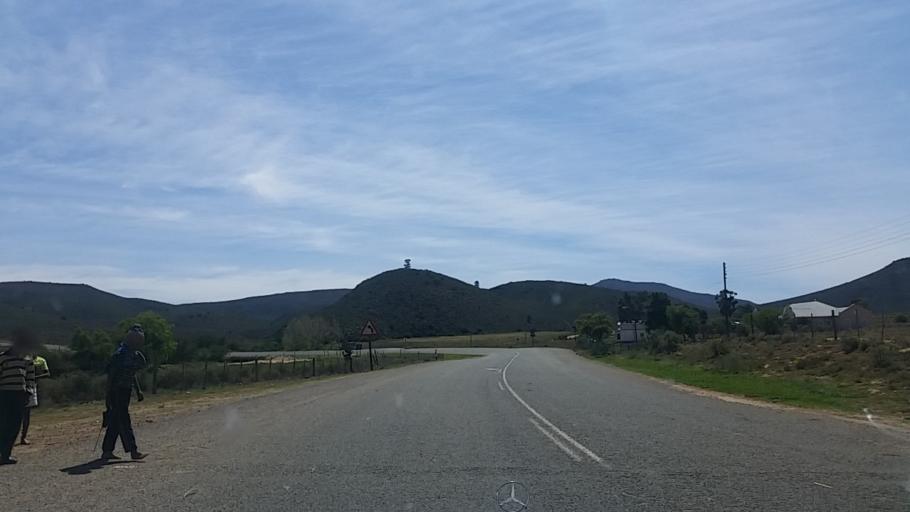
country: ZA
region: Western Cape
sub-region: Eden District Municipality
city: Knysna
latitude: -33.6449
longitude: 23.1372
